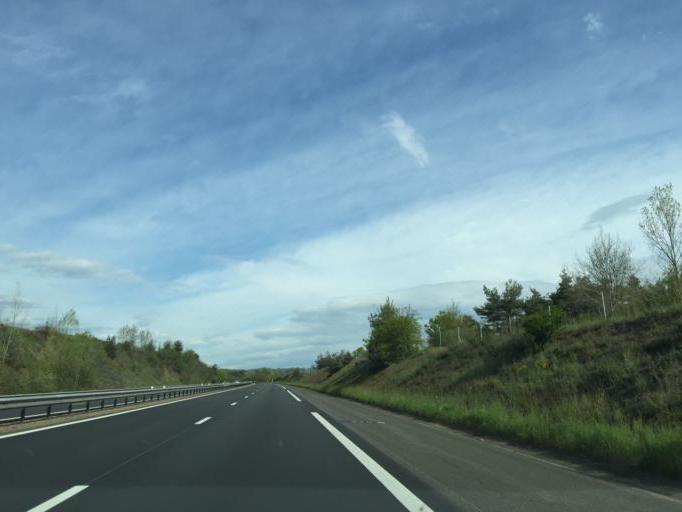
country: FR
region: Rhone-Alpes
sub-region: Departement de la Loire
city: Saint-Germain-Laval
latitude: 45.8641
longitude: 3.9634
